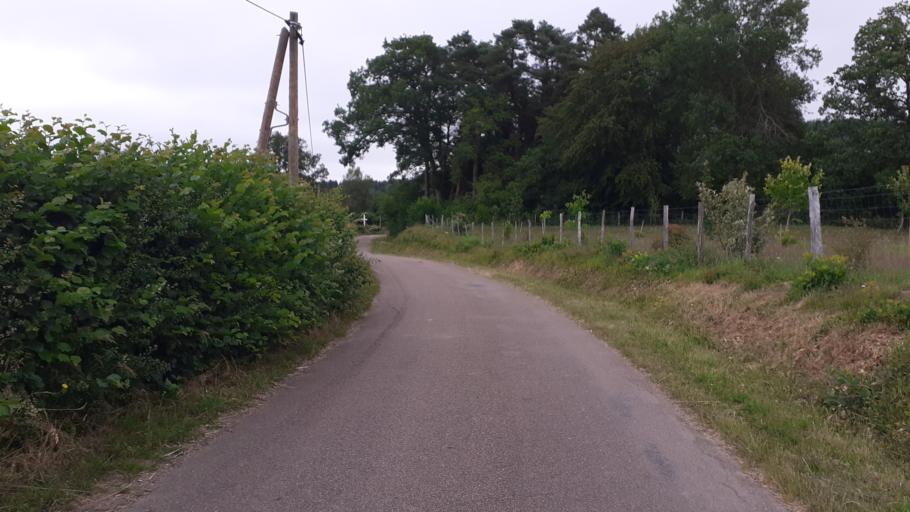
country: FR
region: Bourgogne
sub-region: Departement de la Cote-d'Or
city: Saulieu
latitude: 47.2740
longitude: 4.1412
